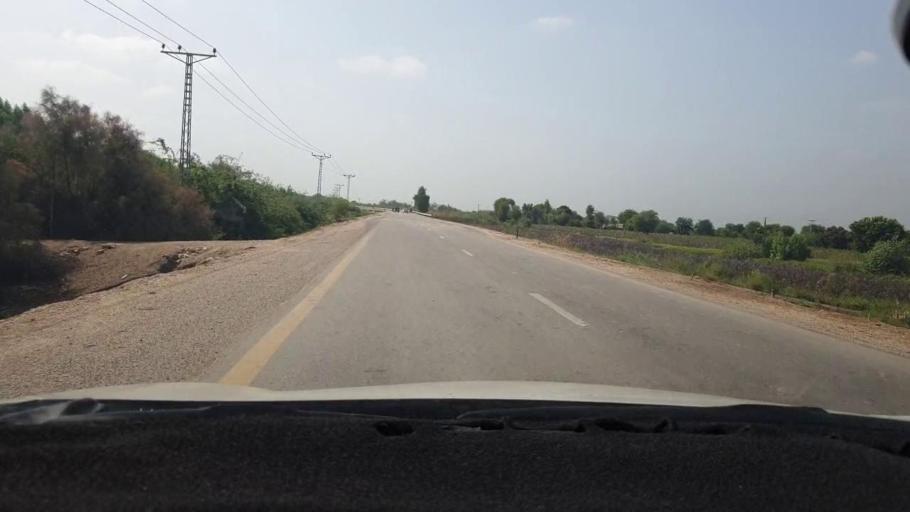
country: PK
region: Sindh
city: Mirpur Khas
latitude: 25.7518
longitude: 69.0845
